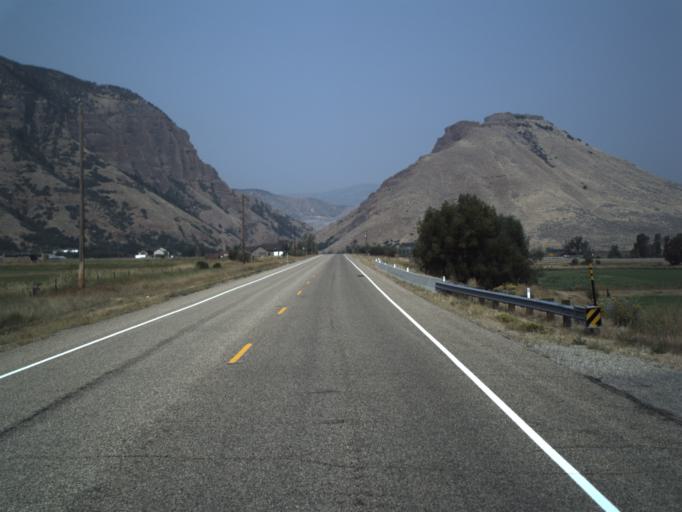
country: US
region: Utah
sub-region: Morgan County
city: Morgan
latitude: 41.0356
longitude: -111.5151
